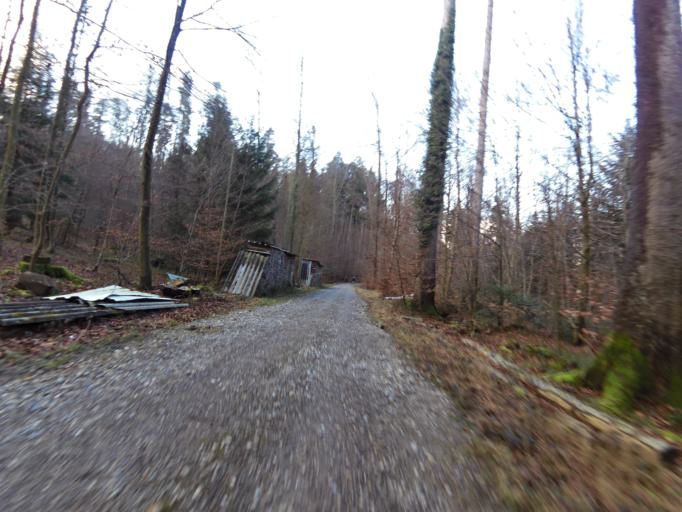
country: CH
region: Zurich
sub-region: Bezirk Dietikon
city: Schlieren / Boden
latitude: 47.3839
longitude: 8.4565
